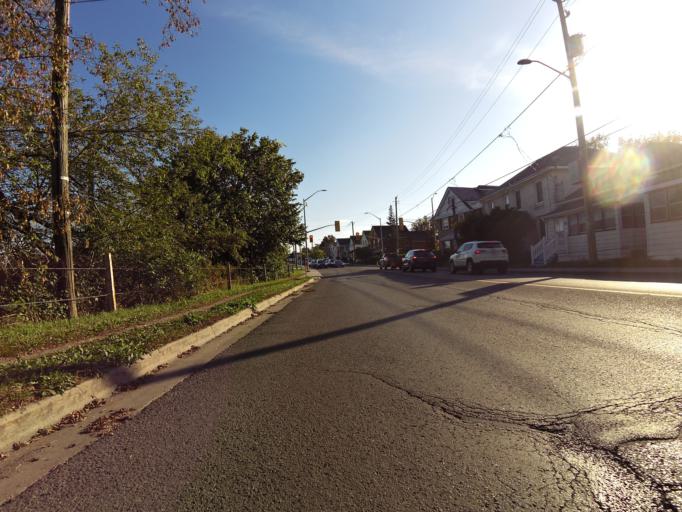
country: CA
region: Ontario
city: Kingston
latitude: 44.2433
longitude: -76.4878
